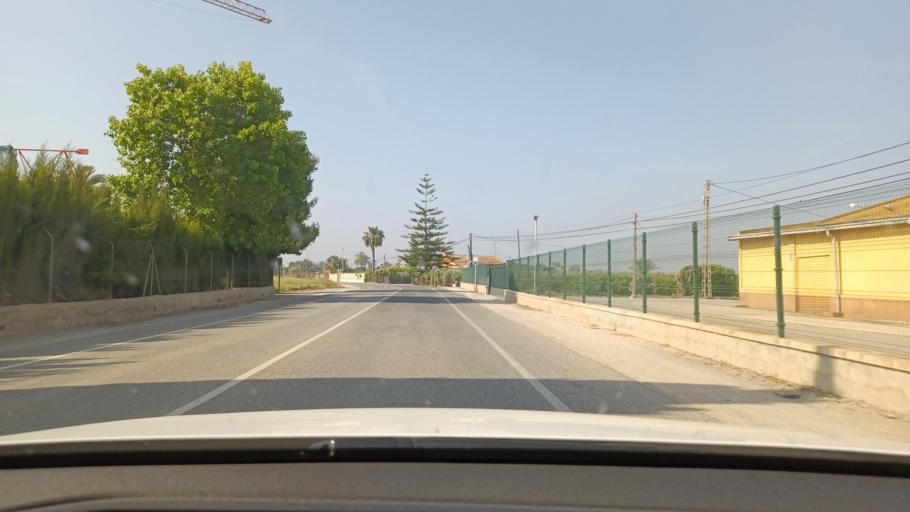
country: ES
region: Valencia
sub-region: Provincia de Alicante
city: Elche
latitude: 38.2324
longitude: -0.7177
